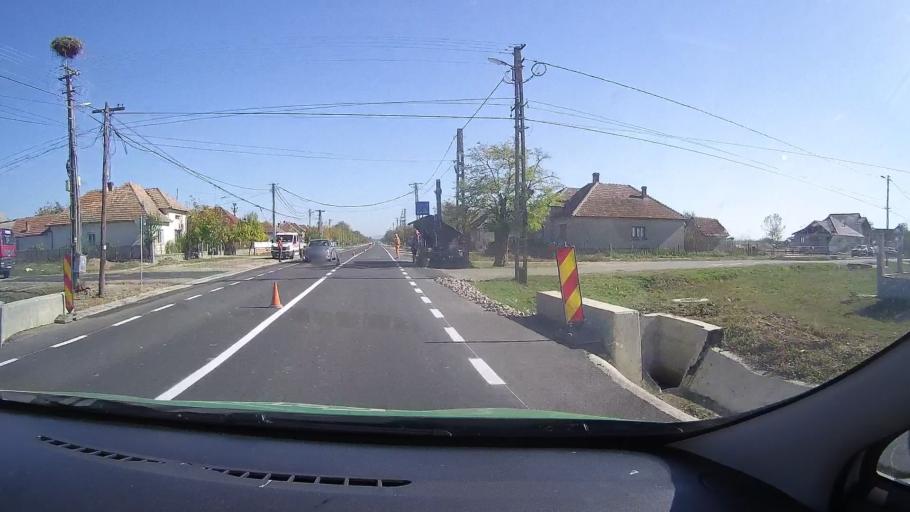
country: RO
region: Satu Mare
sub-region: Oras Ardud
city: Madaras
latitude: 47.6850
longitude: 22.8542
